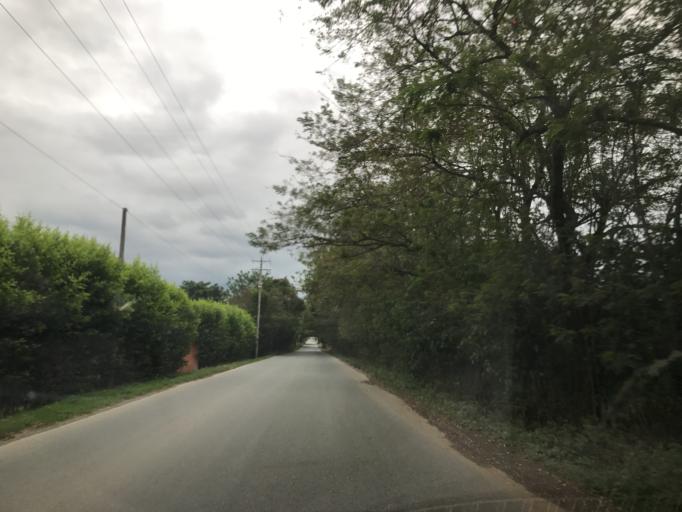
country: CO
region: Quindio
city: Genova
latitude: 4.3453
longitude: -75.7857
